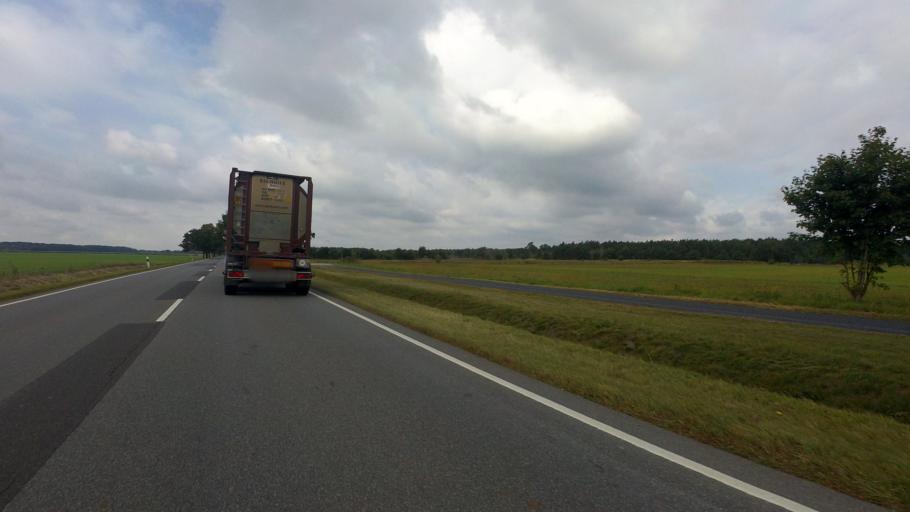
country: DE
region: Brandenburg
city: Schwarzheide
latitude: 51.4707
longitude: 13.8339
